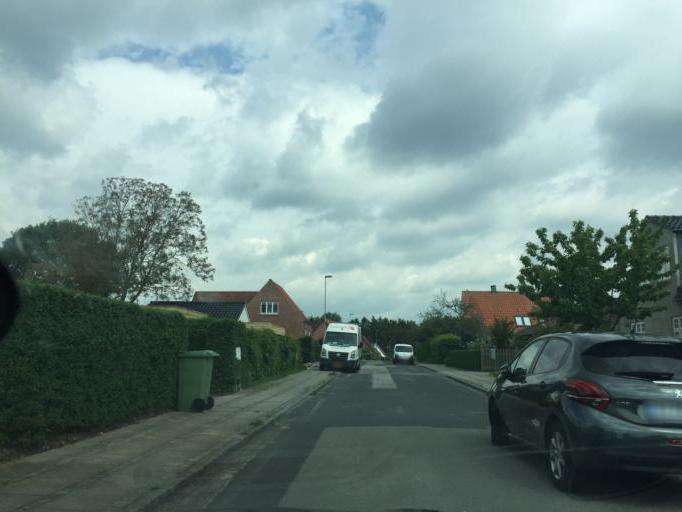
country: DK
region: South Denmark
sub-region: Odense Kommune
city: Odense
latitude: 55.3799
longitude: 10.3531
